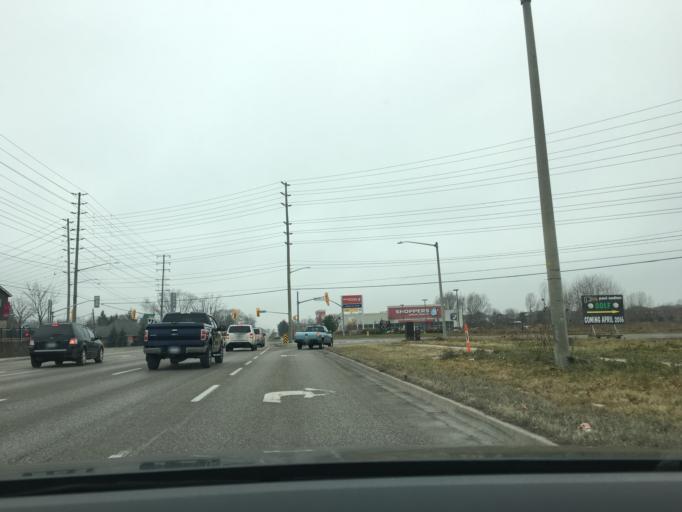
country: CA
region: Ontario
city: Innisfil
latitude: 44.3291
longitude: -79.7136
